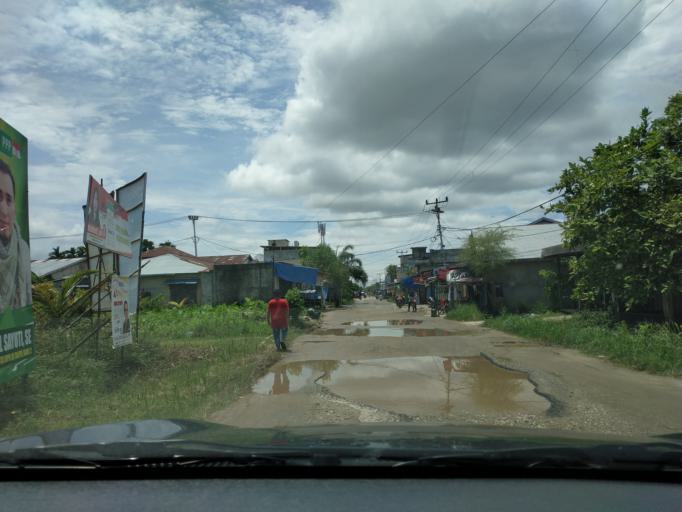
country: ID
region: Riau
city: Tembilahan
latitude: -0.3160
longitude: 103.1698
